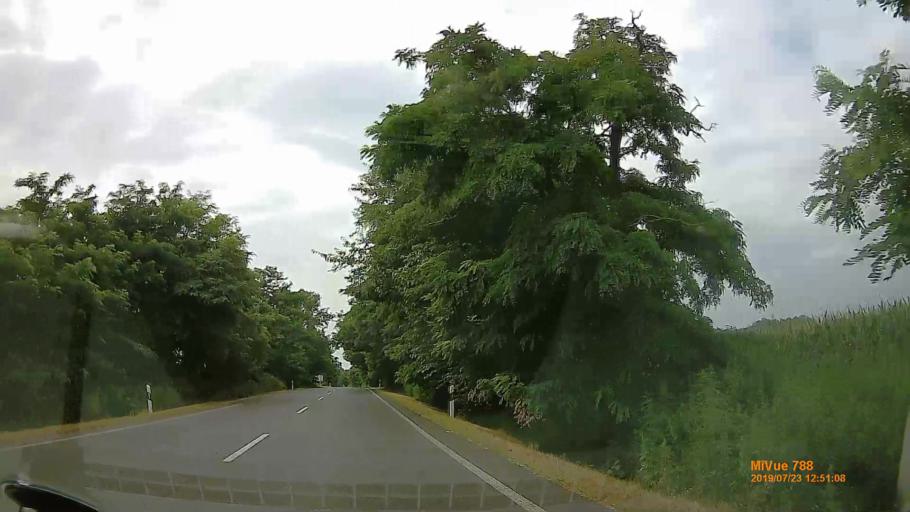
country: HU
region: Szabolcs-Szatmar-Bereg
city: Nagycserkesz
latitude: 47.9578
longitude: 21.5945
